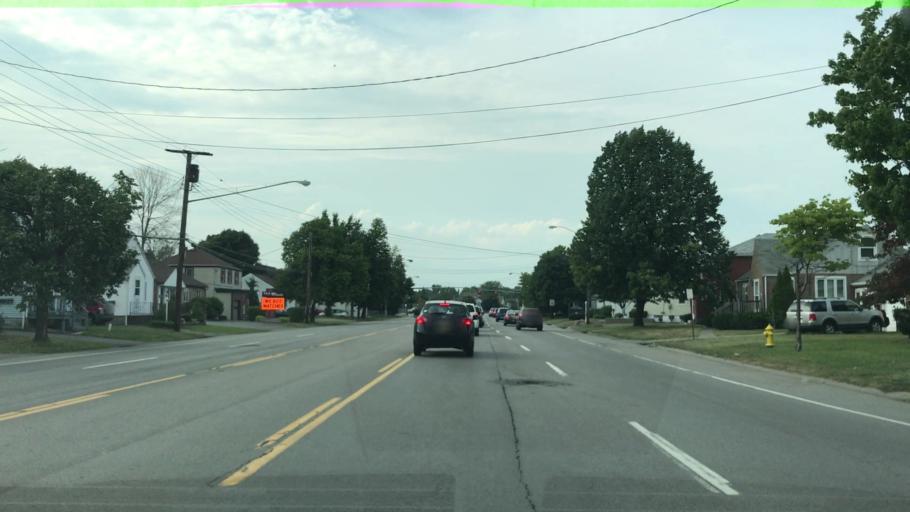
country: US
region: New York
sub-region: Erie County
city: Cheektowaga
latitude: 42.9272
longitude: -78.7430
